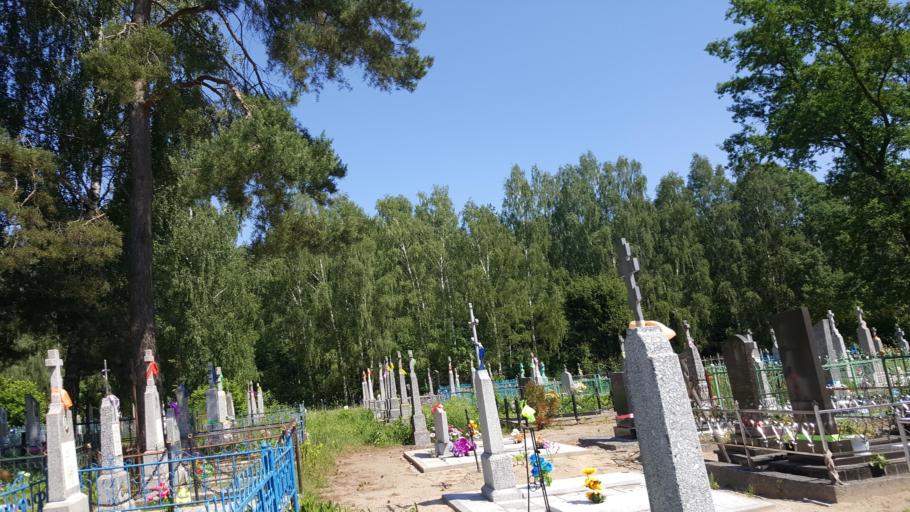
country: BY
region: Brest
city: Zhabinka
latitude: 52.2441
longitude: 24.0098
